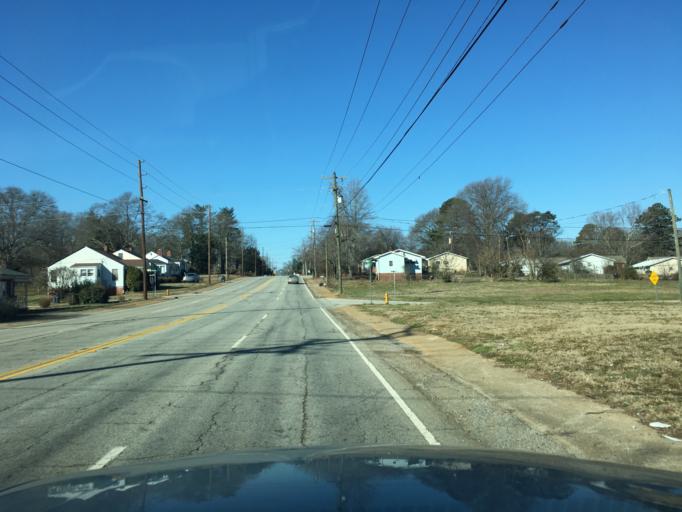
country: US
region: South Carolina
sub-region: Greenville County
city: Sans Souci
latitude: 34.8934
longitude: -82.4258
